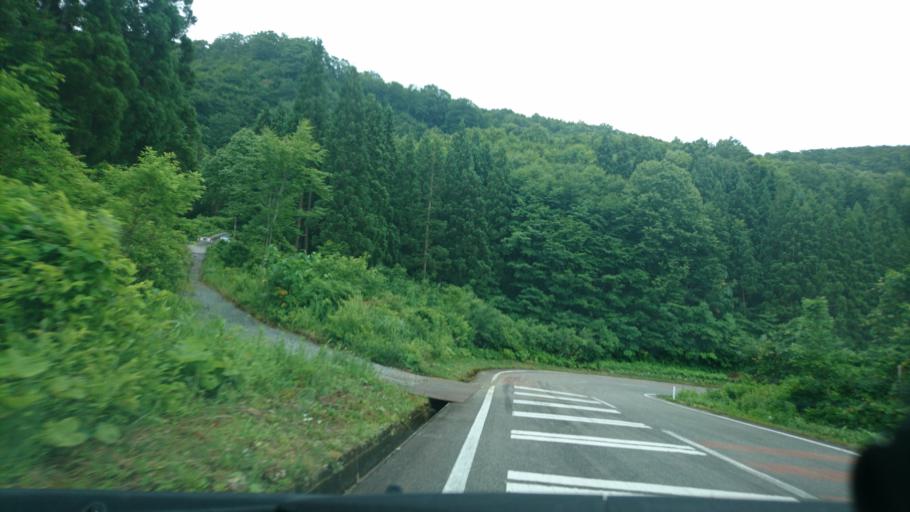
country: JP
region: Akita
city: Yuzawa
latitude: 39.1564
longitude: 140.7489
